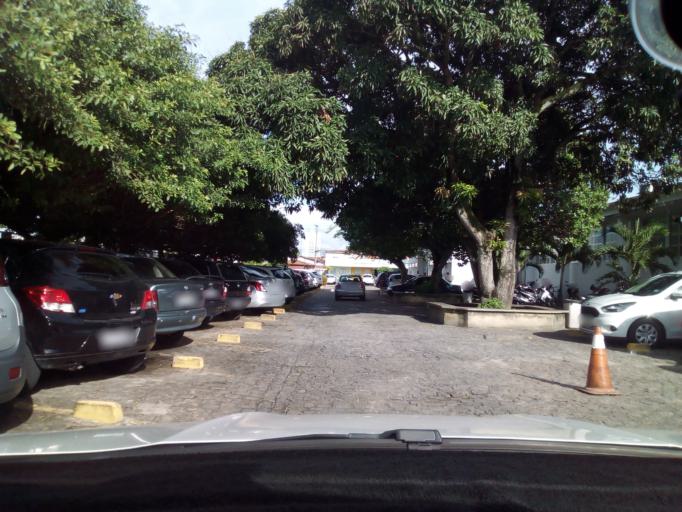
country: BR
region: Paraiba
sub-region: Joao Pessoa
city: Joao Pessoa
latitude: -7.1315
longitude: -34.8738
